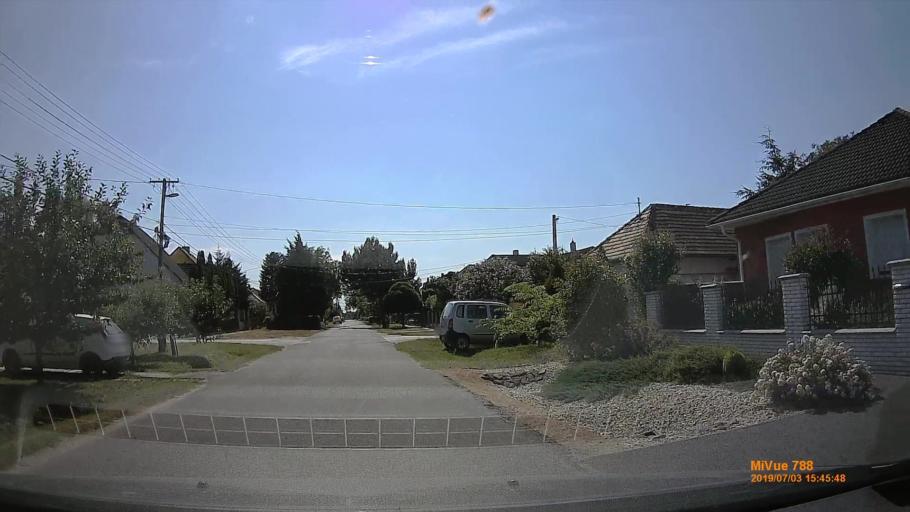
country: HU
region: Gyor-Moson-Sopron
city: Toltestava
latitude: 47.6926
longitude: 17.7546
